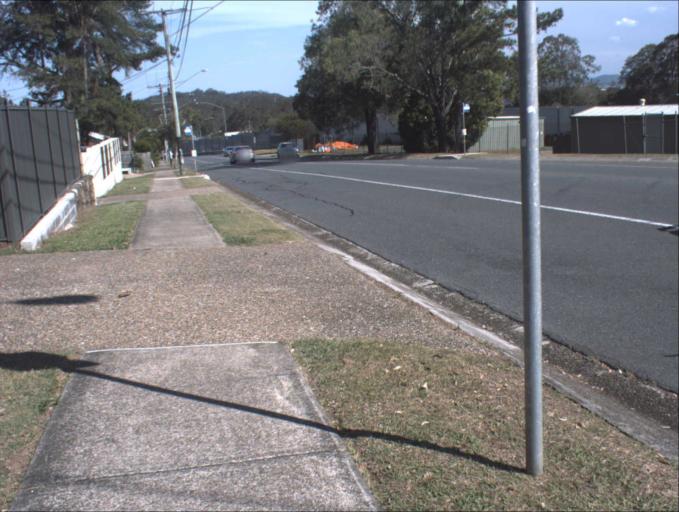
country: AU
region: Queensland
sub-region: Logan
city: Slacks Creek
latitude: -27.6450
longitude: 153.1496
